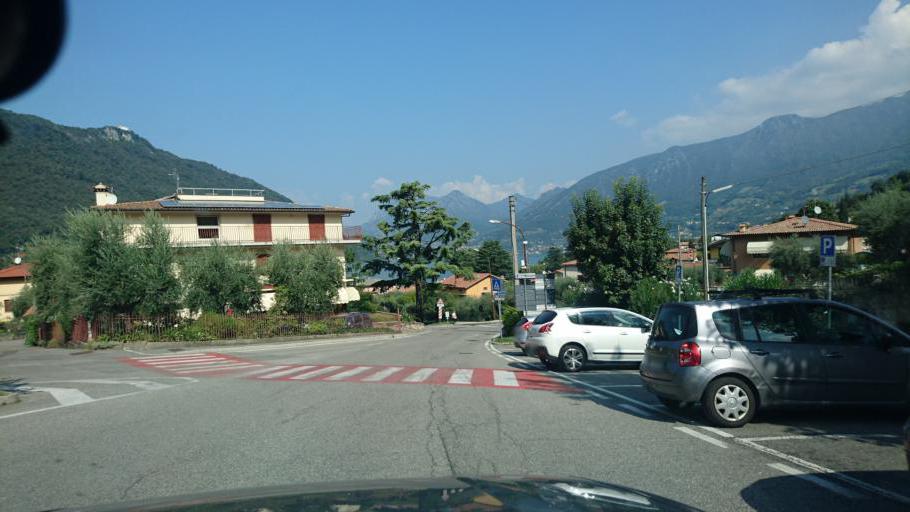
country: IT
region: Lombardy
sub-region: Provincia di Brescia
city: Sulzano
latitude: 45.6892
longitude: 10.1023
